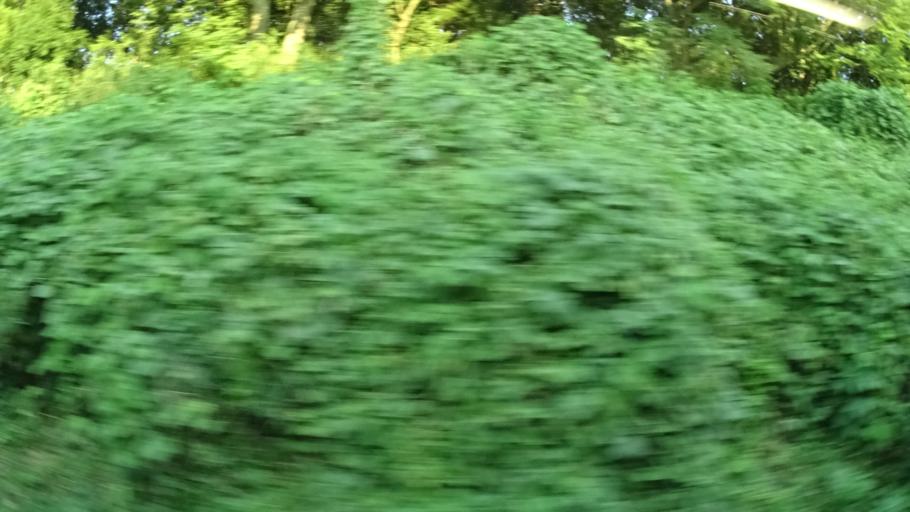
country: JP
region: Ibaraki
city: Ishioka
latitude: 36.1466
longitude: 140.2841
